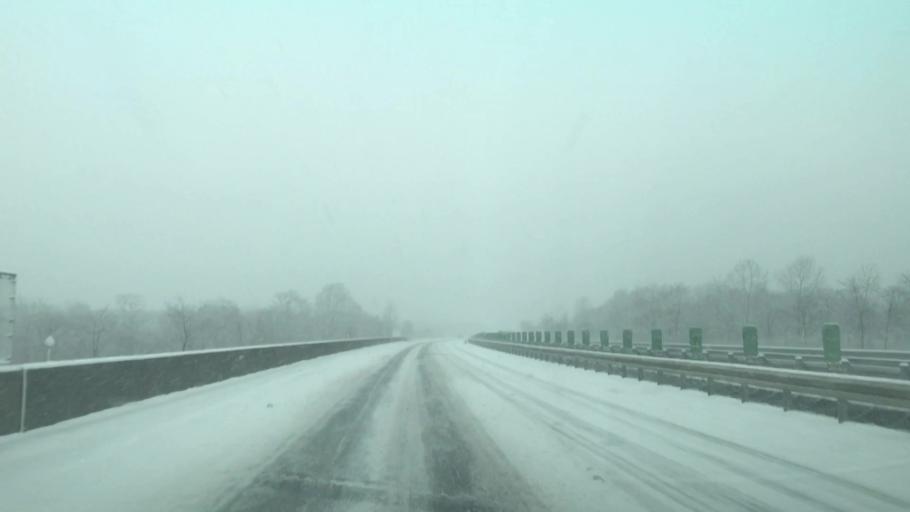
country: JP
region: Hokkaido
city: Shiraoi
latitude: 42.5111
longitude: 141.2700
